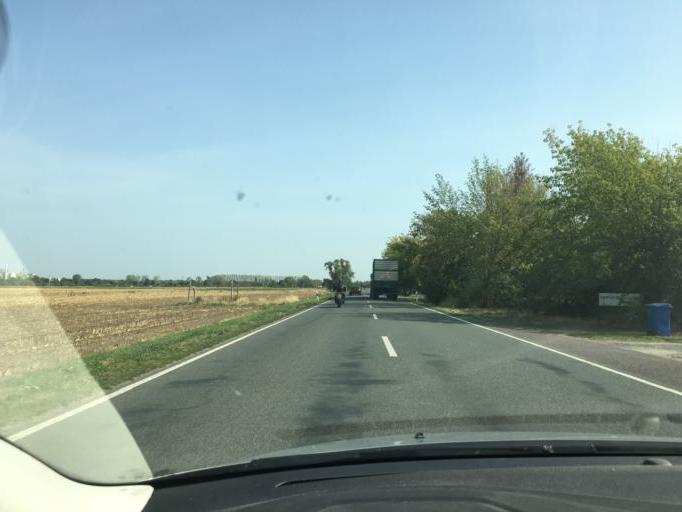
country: DE
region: Saxony-Anhalt
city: Barby
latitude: 51.9844
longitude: 11.8563
